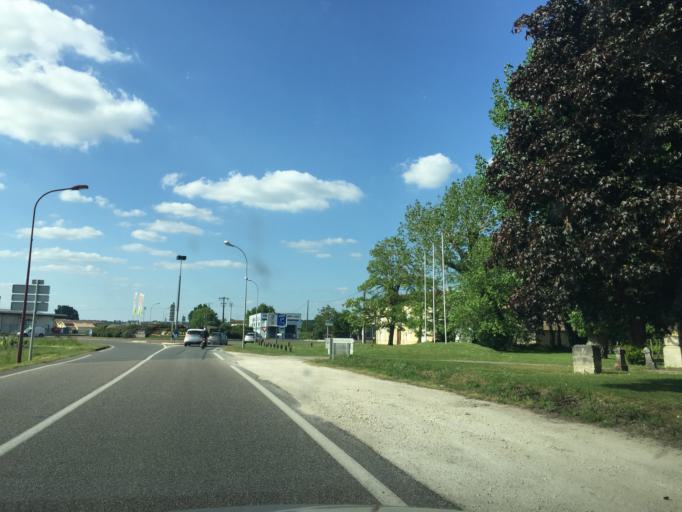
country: FR
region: Aquitaine
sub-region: Departement de la Gironde
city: Sainte-Terre
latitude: 44.8477
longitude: -0.1465
